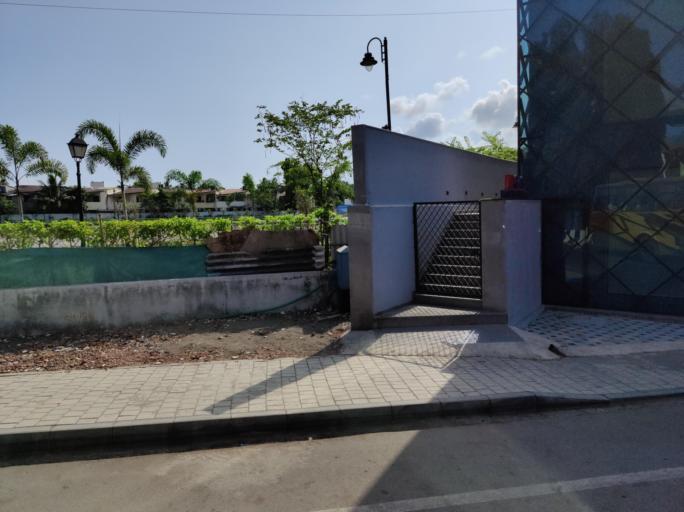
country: IN
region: Daman and Diu
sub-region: Daman District
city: Daman
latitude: 20.4187
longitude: 72.8370
